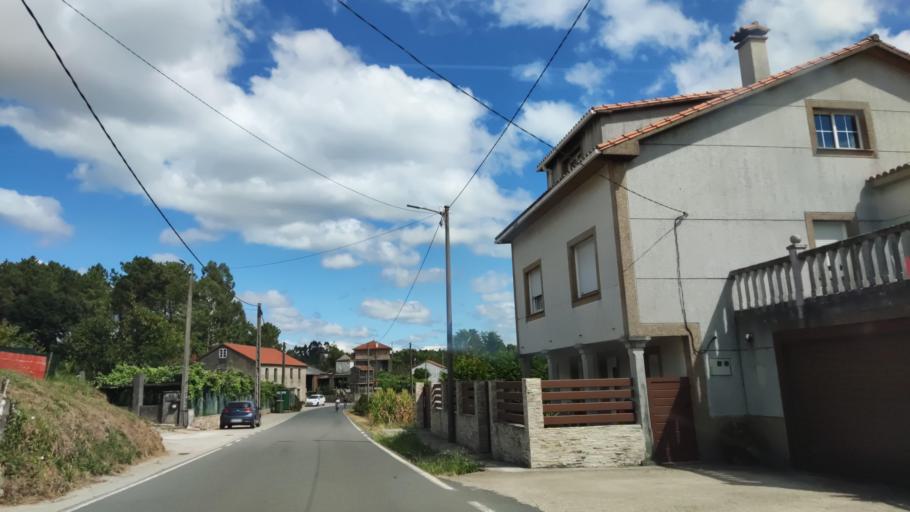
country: ES
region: Galicia
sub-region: Provincia da Coruna
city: Rois
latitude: 42.7790
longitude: -8.6694
